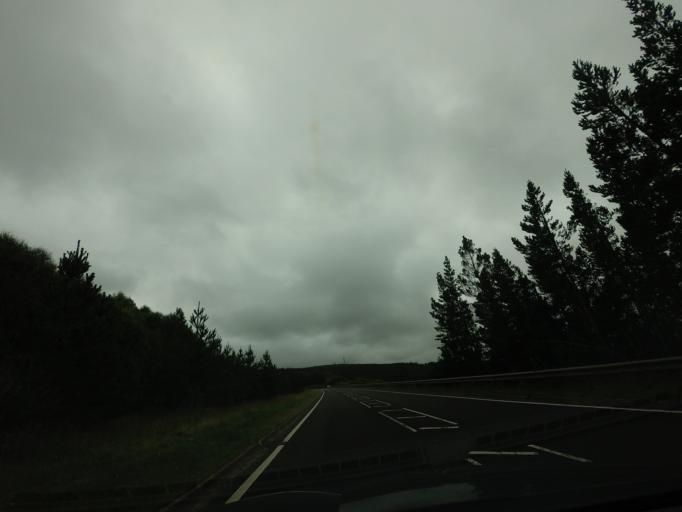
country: GB
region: Scotland
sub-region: Highland
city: Aviemore
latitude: 57.2932
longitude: -3.9160
